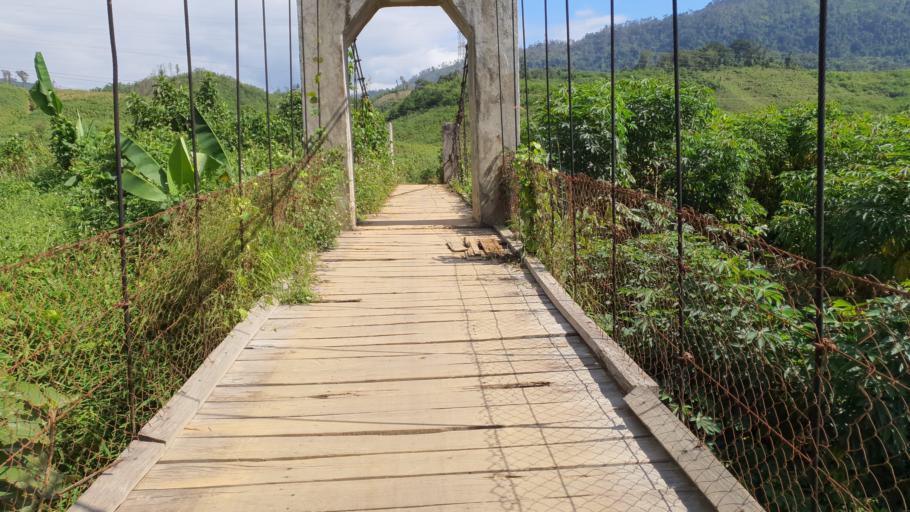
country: LA
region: Bolikhamxai
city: Bolikhan
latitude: 18.9098
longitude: 103.7431
